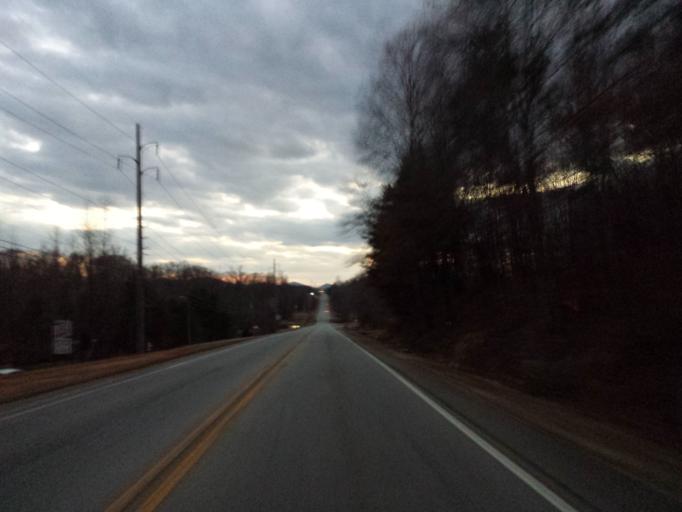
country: US
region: Georgia
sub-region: White County
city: Cleveland
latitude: 34.6442
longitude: -83.7381
